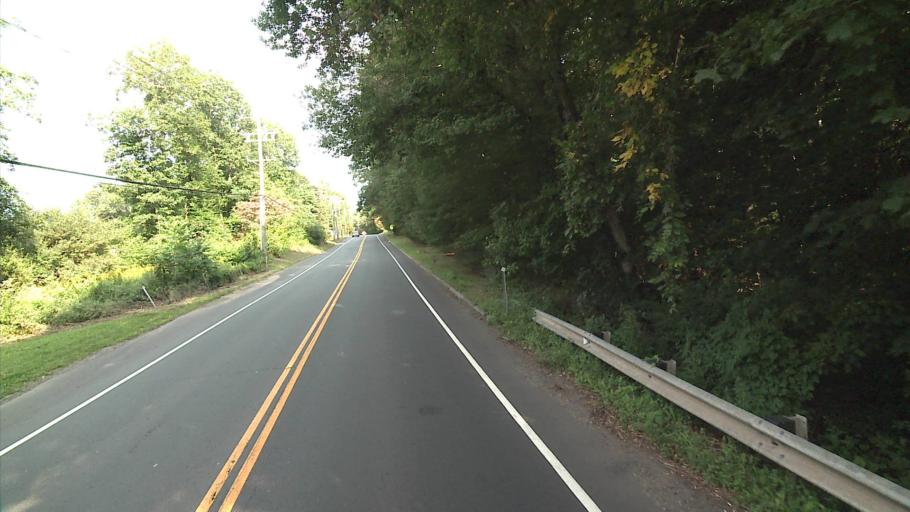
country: US
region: Connecticut
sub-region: Fairfield County
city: New Canaan
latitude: 41.1444
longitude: -73.4791
